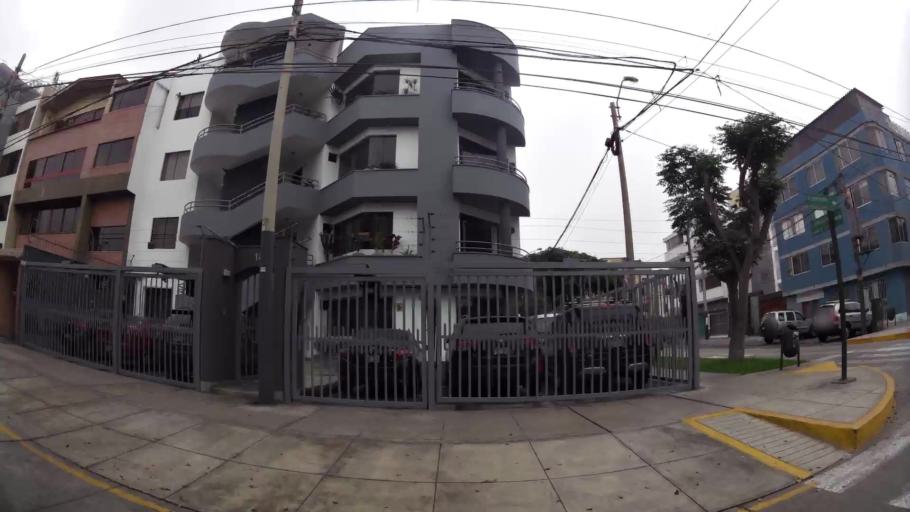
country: PE
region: Lima
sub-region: Lima
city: Surco
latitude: -12.1365
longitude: -76.9901
